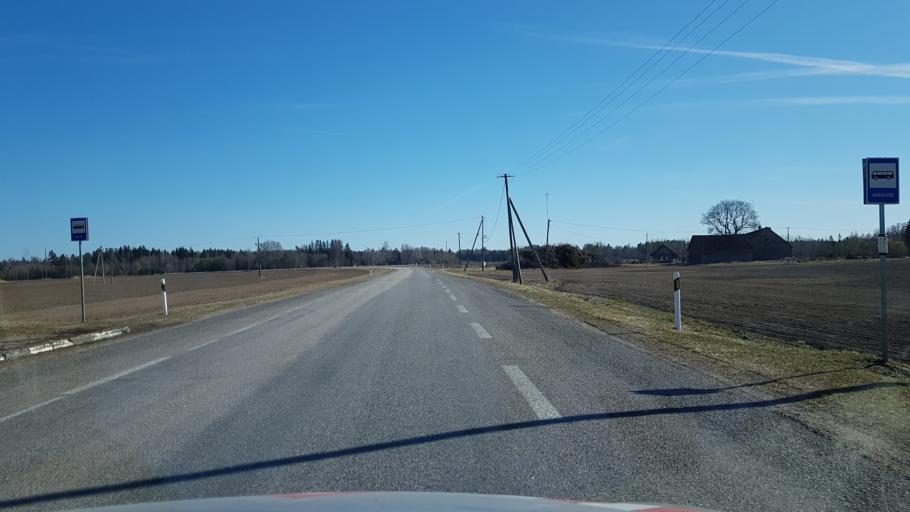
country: EE
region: Laeaene-Virumaa
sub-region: Vinni vald
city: Vinni
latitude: 59.2378
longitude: 26.6939
